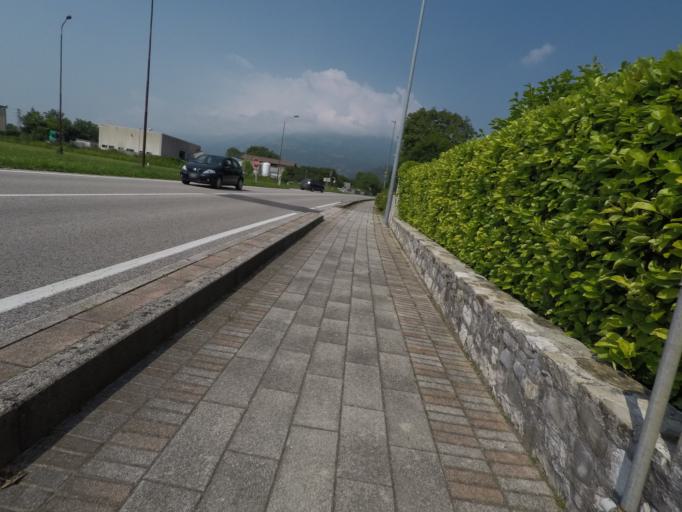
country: IT
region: Friuli Venezia Giulia
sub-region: Provincia di Pordenone
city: Vajont
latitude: 46.1605
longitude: 12.6856
